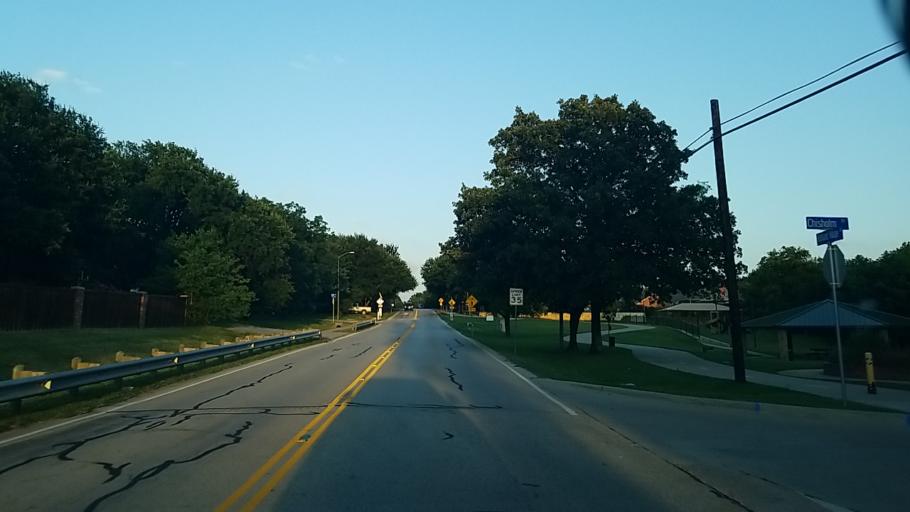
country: US
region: Texas
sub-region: Denton County
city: Highland Village
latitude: 33.0931
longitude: -97.0396
